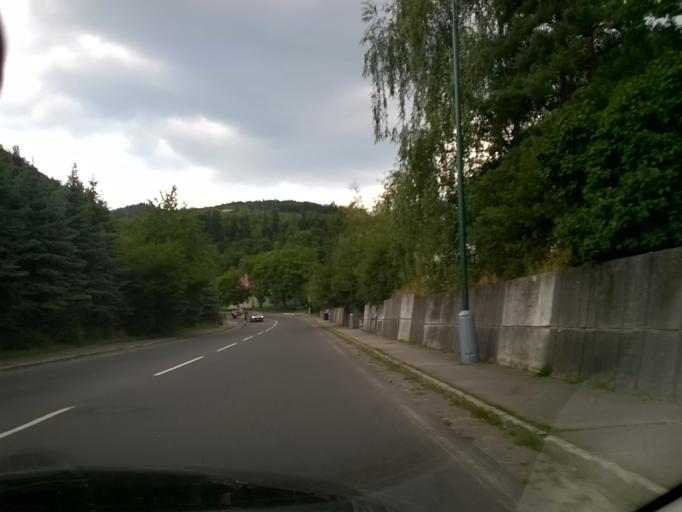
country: SK
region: Banskobystricky
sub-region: Okres Banska Bystrica
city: Banska Stiavnica
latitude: 48.4633
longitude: 18.9030
